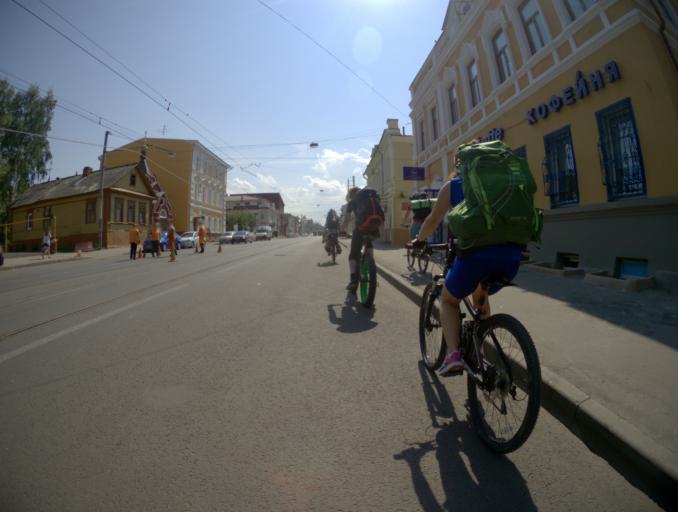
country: RU
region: Nizjnij Novgorod
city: Nizhniy Novgorod
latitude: 56.3176
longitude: 43.9882
